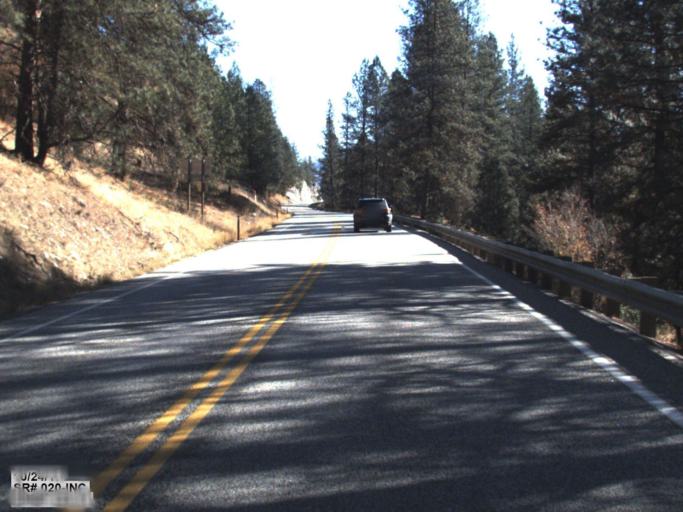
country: US
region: Washington
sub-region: Stevens County
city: Kettle Falls
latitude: 48.5900
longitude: -118.1593
